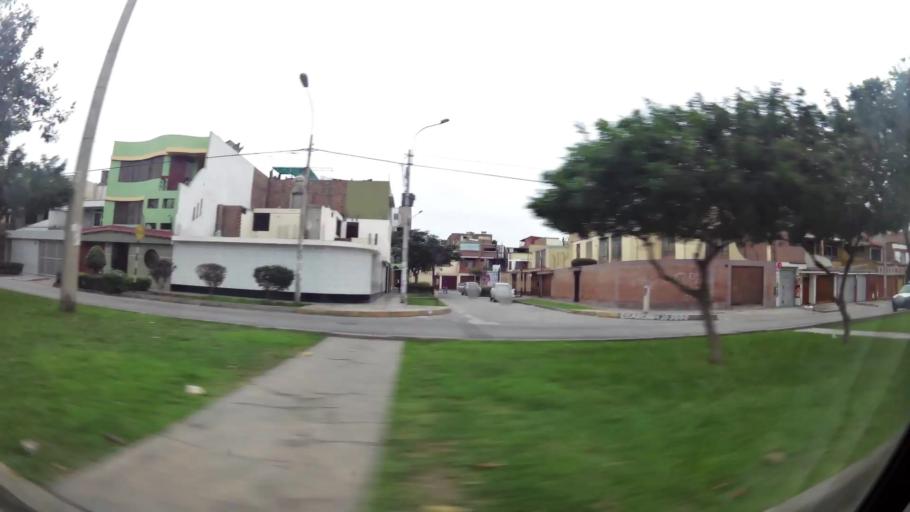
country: PE
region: Lima
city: Lima
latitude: -12.0655
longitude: -77.0672
